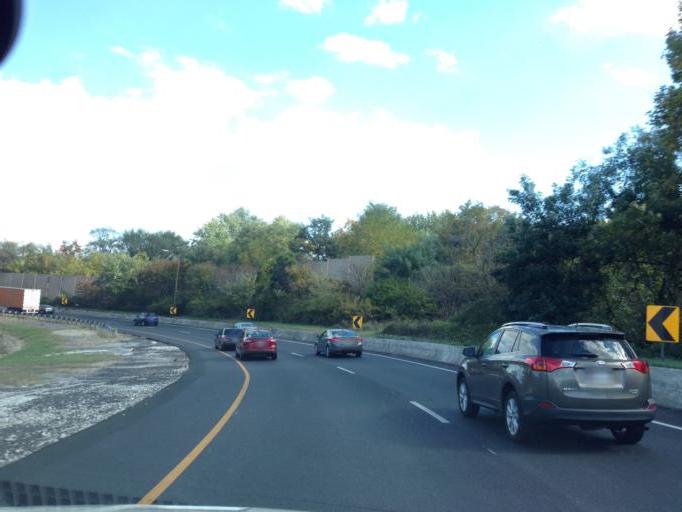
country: US
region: Maryland
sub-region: Baltimore County
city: Mays Chapel
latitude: 39.4200
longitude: -76.6420
